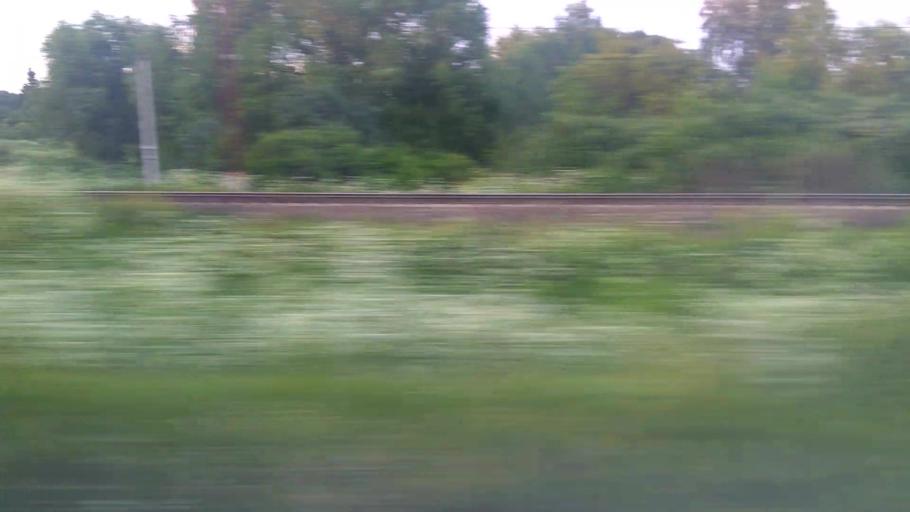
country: RU
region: Moskovskaya
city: Barybino
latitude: 55.2794
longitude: 37.8929
